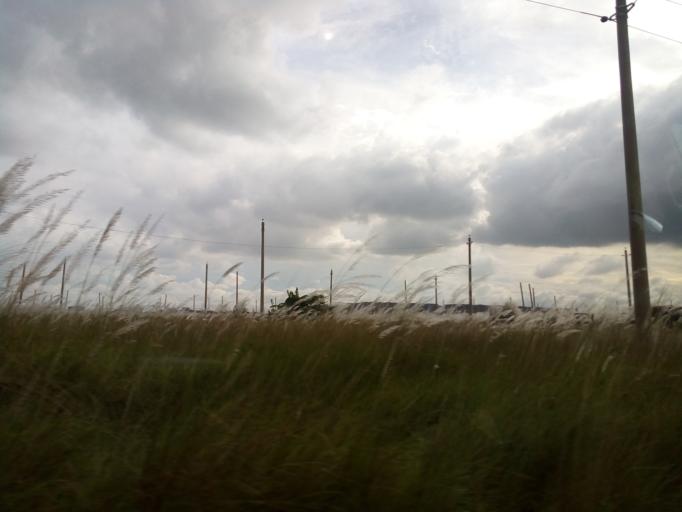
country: BD
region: Dhaka
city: Tungi
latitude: 23.8684
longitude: 90.3644
